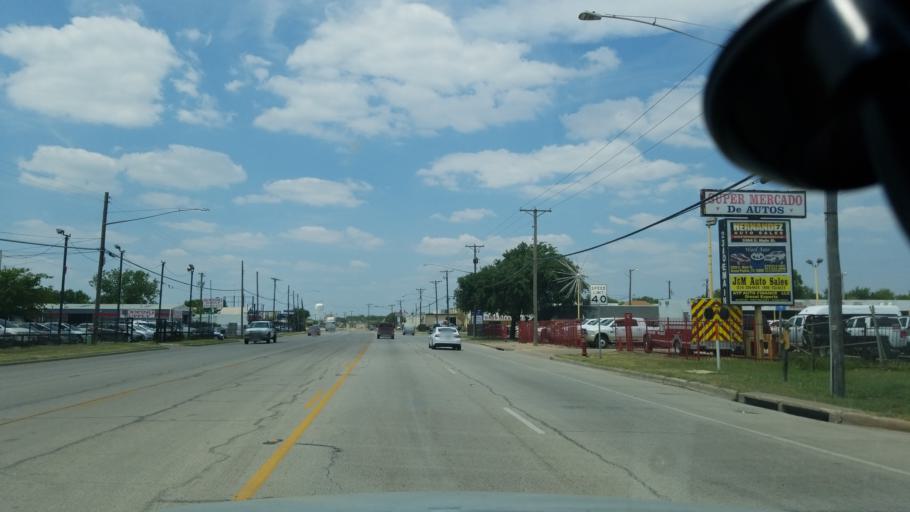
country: US
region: Texas
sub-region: Dallas County
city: Grand Prairie
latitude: 32.7494
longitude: -96.9718
